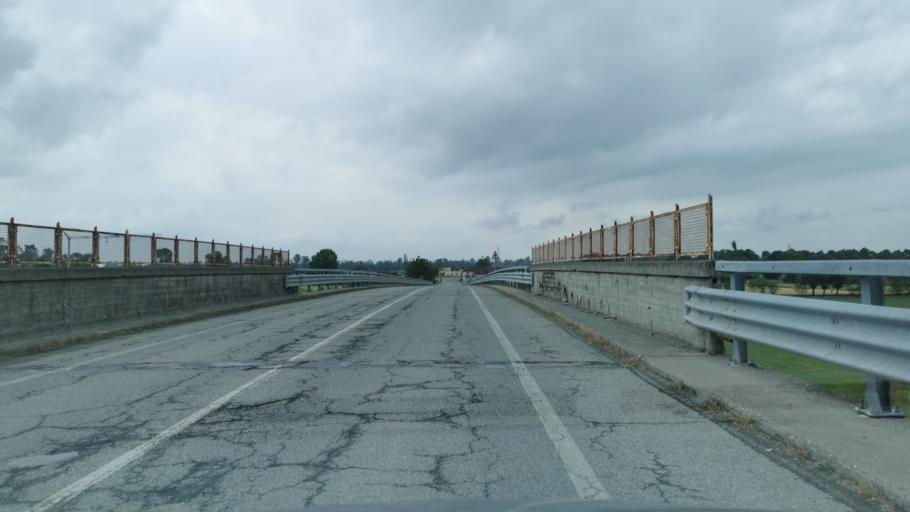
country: IT
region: Piedmont
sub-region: Provincia di Cuneo
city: Savigliano
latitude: 44.6373
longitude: 7.6425
